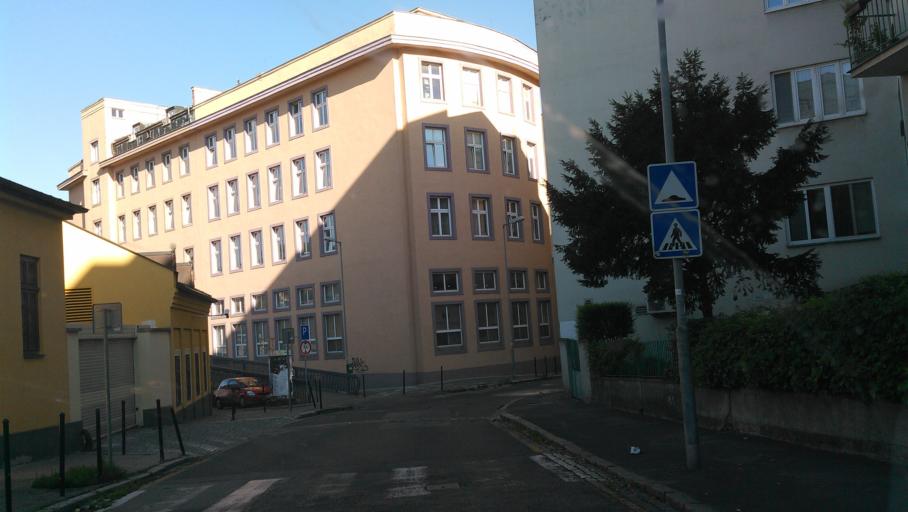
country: SK
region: Bratislavsky
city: Bratislava
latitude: 48.1551
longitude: 17.1044
